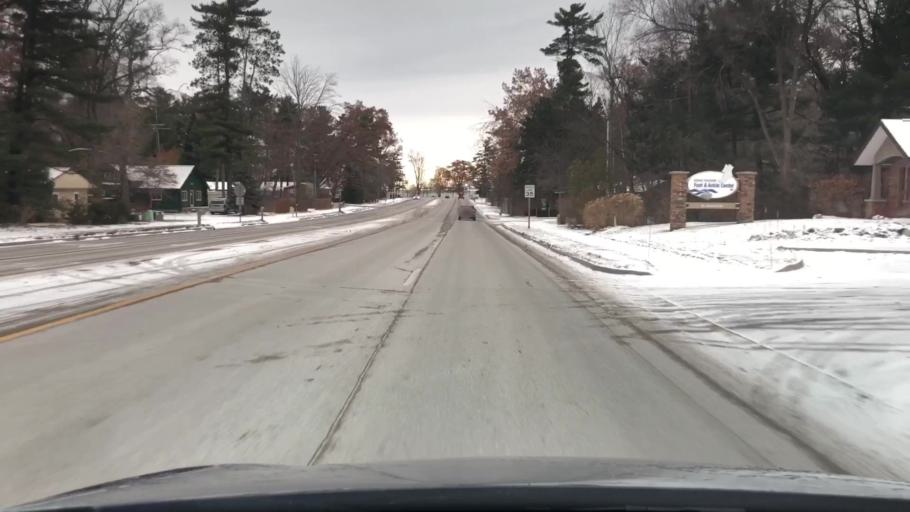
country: US
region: Michigan
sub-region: Grand Traverse County
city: Traverse City
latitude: 44.7461
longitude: -85.5603
